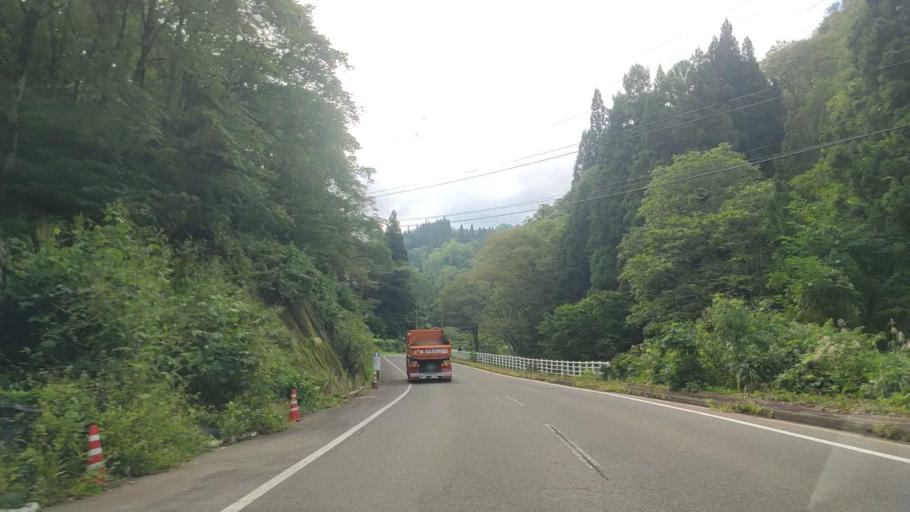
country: JP
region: Nagano
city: Iiyama
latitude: 36.9069
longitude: 138.3145
